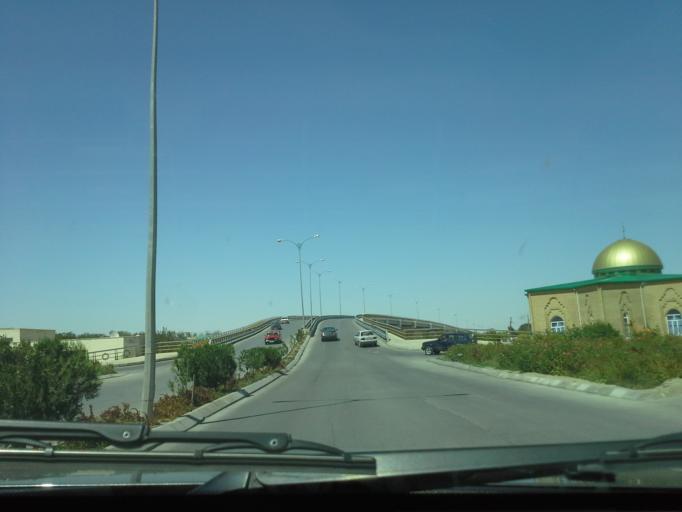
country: TM
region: Balkan
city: Serdar
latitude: 38.9768
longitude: 56.2779
